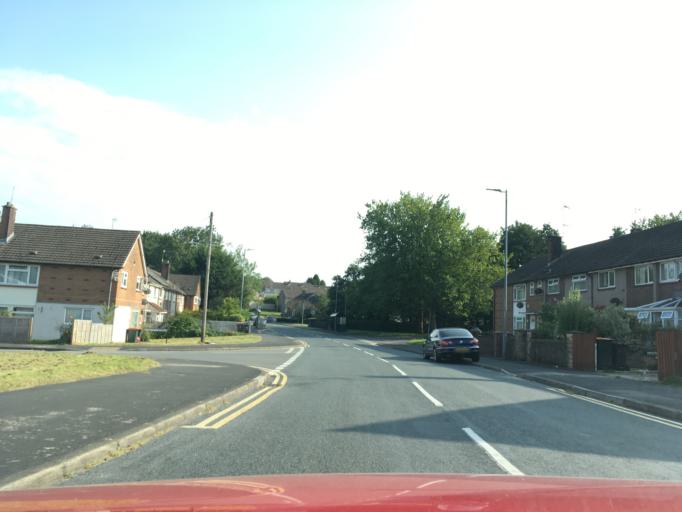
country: GB
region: Wales
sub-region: Newport
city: Newport
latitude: 51.6079
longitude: -3.0357
